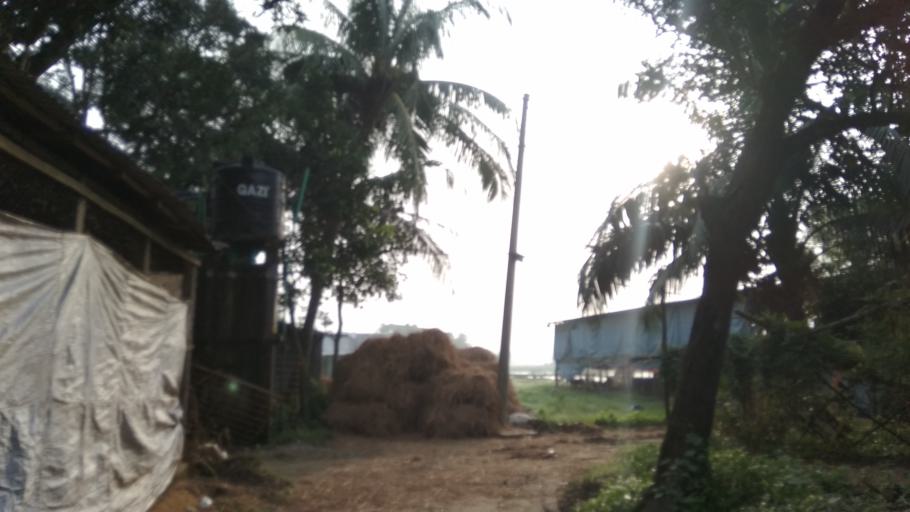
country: BD
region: Dhaka
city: Tungi
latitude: 23.8525
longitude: 90.4427
